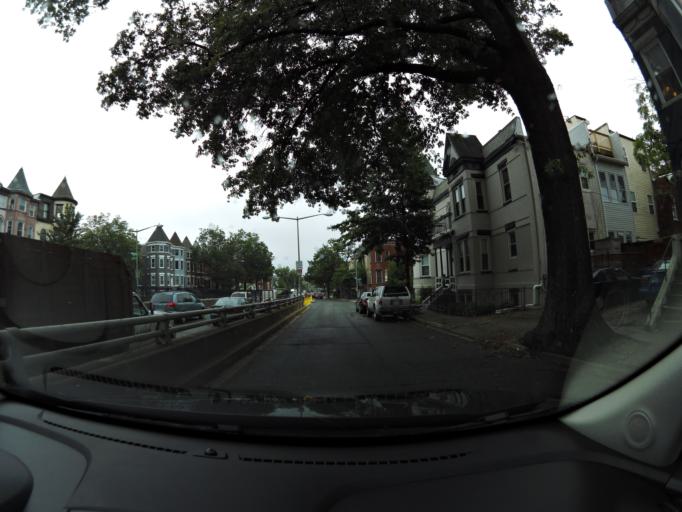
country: US
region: Washington, D.C.
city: Washington, D.C.
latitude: 38.9145
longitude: -77.0092
